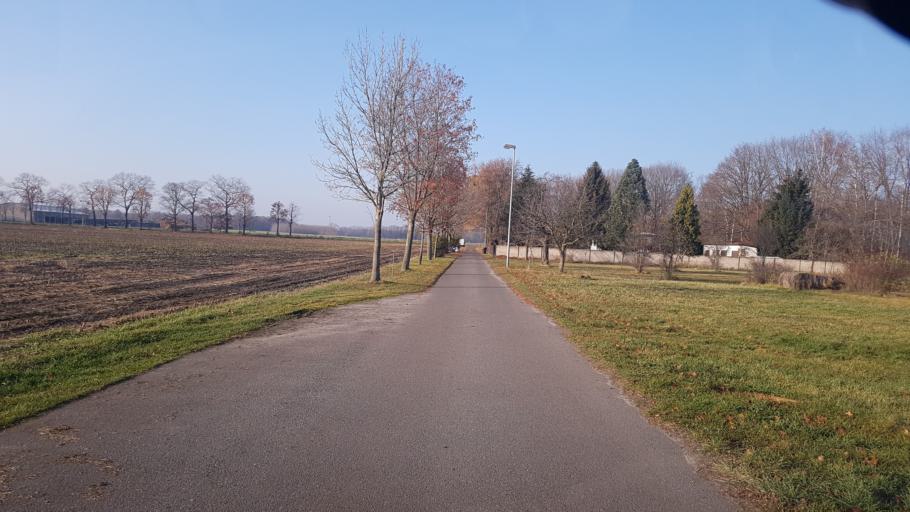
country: DE
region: Brandenburg
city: Tettau
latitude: 51.4359
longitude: 13.7344
